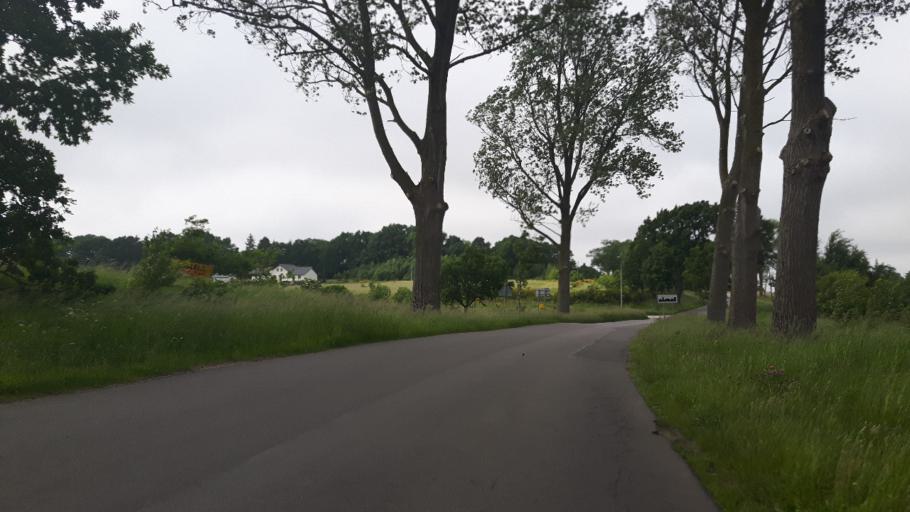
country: PL
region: Pomeranian Voivodeship
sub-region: Slupsk
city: Slupsk
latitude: 54.6281
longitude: 17.0229
